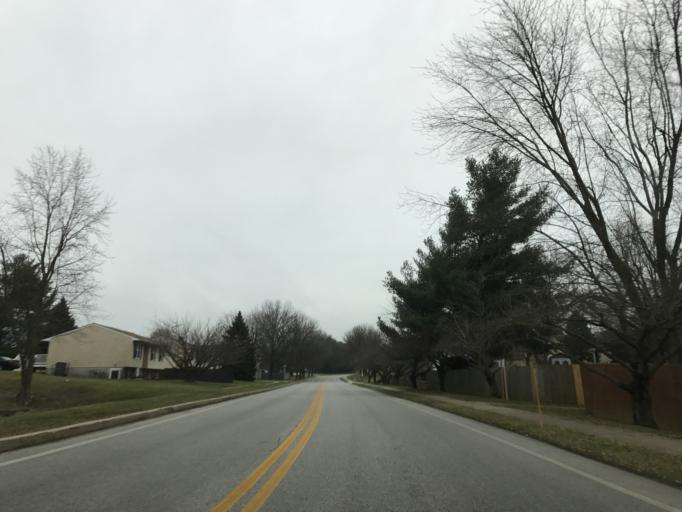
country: US
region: Maryland
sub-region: Carroll County
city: Westminster
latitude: 39.5667
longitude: -76.9956
